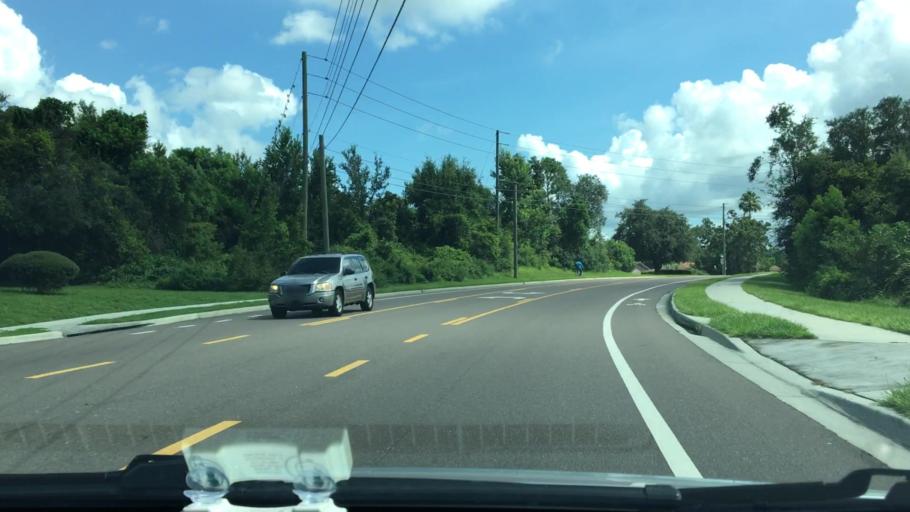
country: US
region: Florida
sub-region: Volusia County
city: Deltona
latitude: 28.8890
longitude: -81.2190
